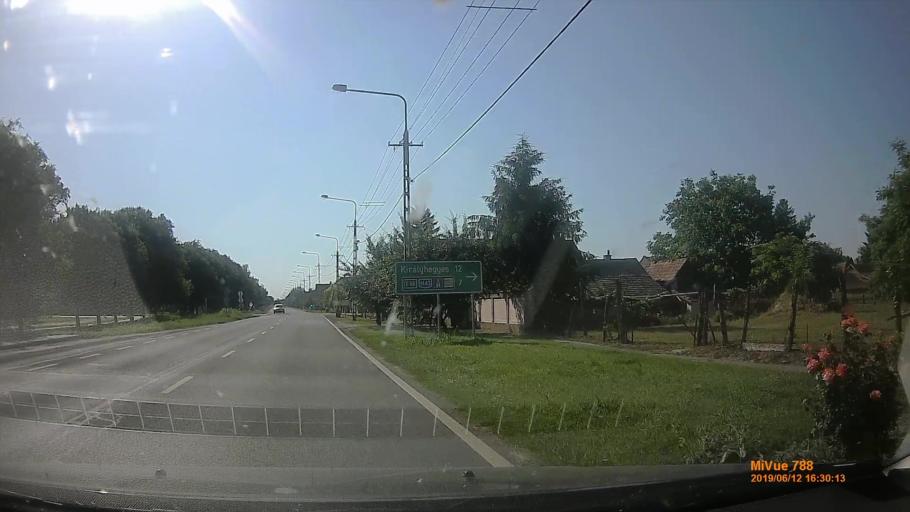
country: HU
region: Csongrad
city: Apatfalva
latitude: 46.1726
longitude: 20.5874
